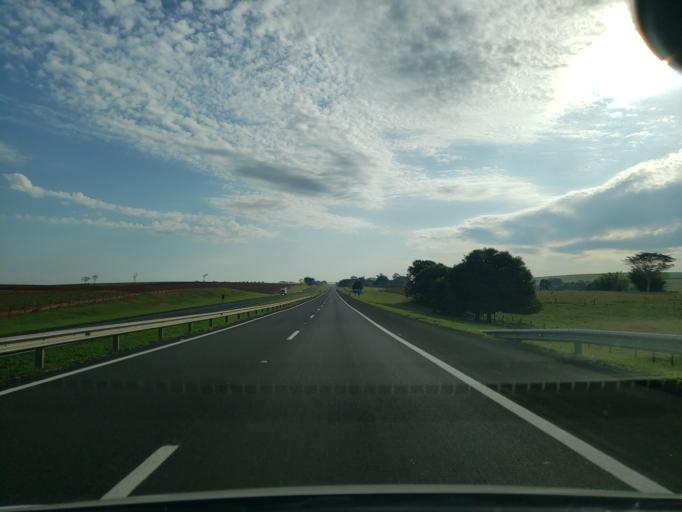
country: BR
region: Sao Paulo
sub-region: Valparaiso
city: Valparaiso
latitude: -21.2063
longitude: -50.7694
